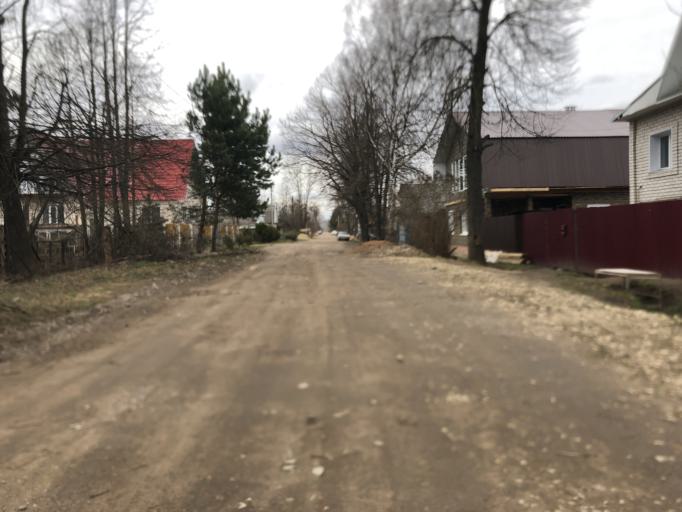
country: RU
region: Tverskaya
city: Rzhev
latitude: 56.2488
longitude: 34.3168
